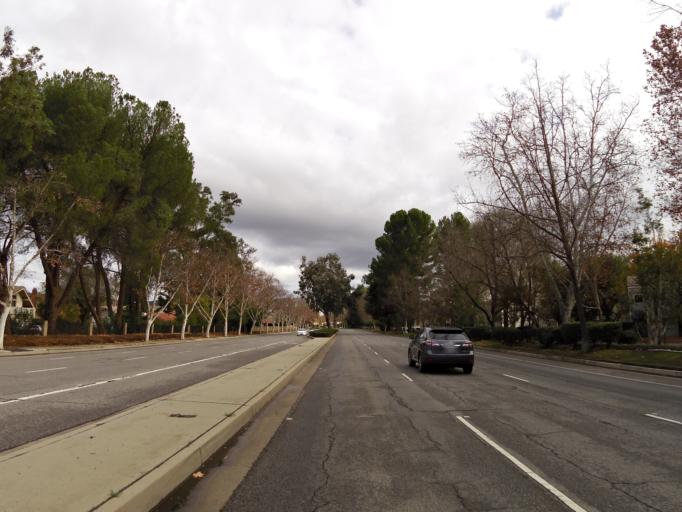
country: US
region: California
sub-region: Ventura County
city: Thousand Oaks
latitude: 34.1498
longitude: -118.8365
